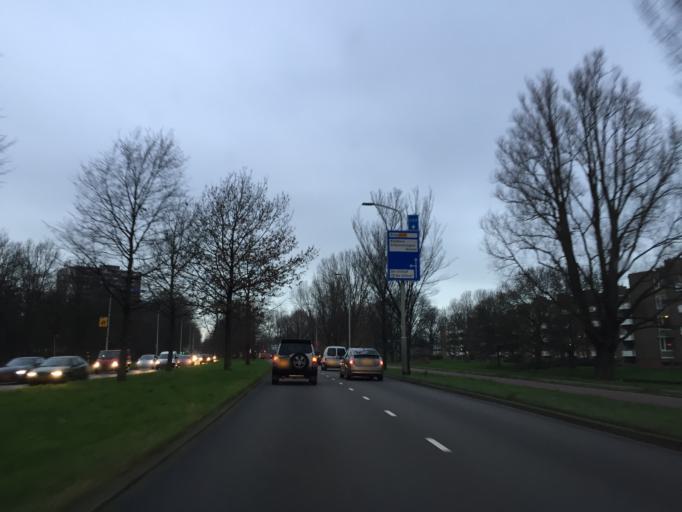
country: NL
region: South Holland
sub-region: Gemeente Westland
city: Kwintsheul
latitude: 52.0386
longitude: 4.2500
